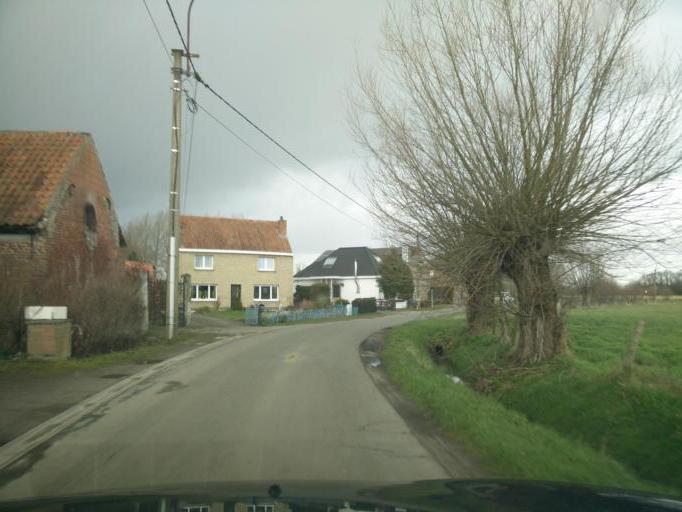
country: BE
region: Flanders
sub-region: Provincie Oost-Vlaanderen
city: Laarne
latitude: 51.0389
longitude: 3.8284
